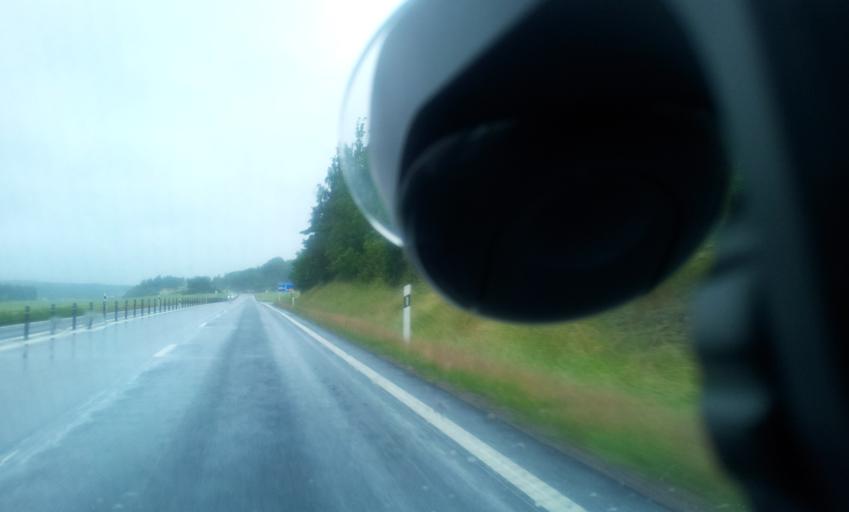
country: SE
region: OEstergoetland
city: Lindo
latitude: 58.5482
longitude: 16.2581
